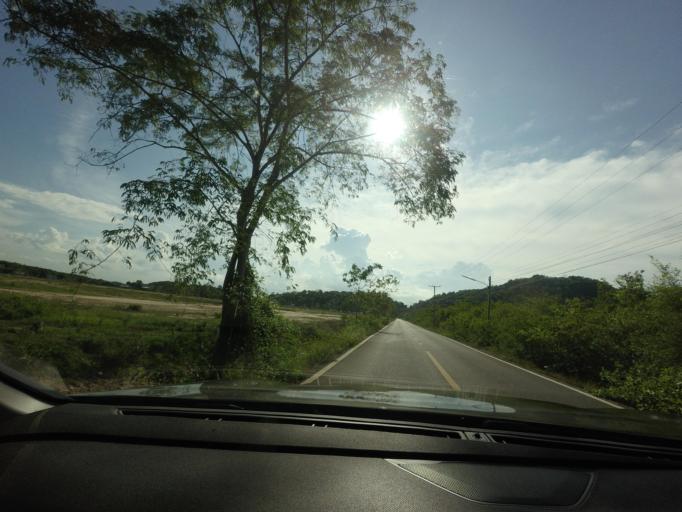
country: TH
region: Prachuap Khiri Khan
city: Pran Buri
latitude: 12.4090
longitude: 99.9834
